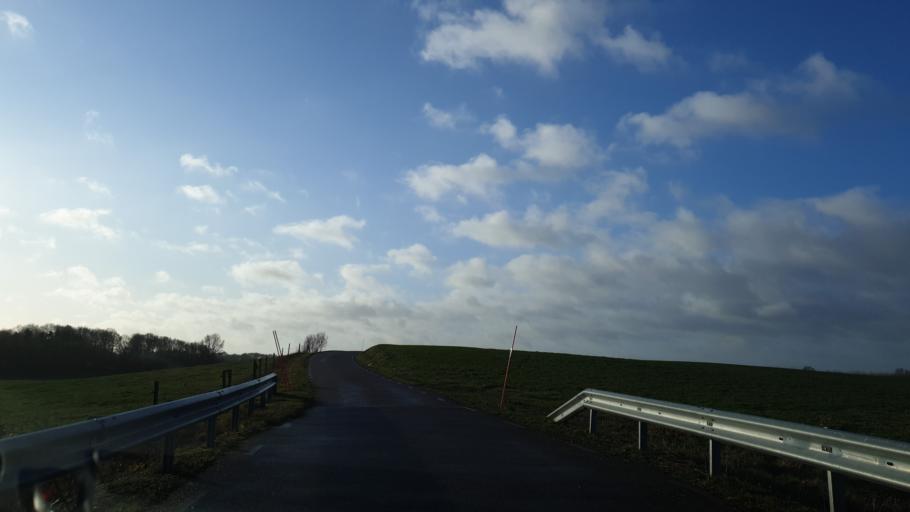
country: SE
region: Skane
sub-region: Svedala Kommun
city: Svedala
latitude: 55.5003
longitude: 13.2921
